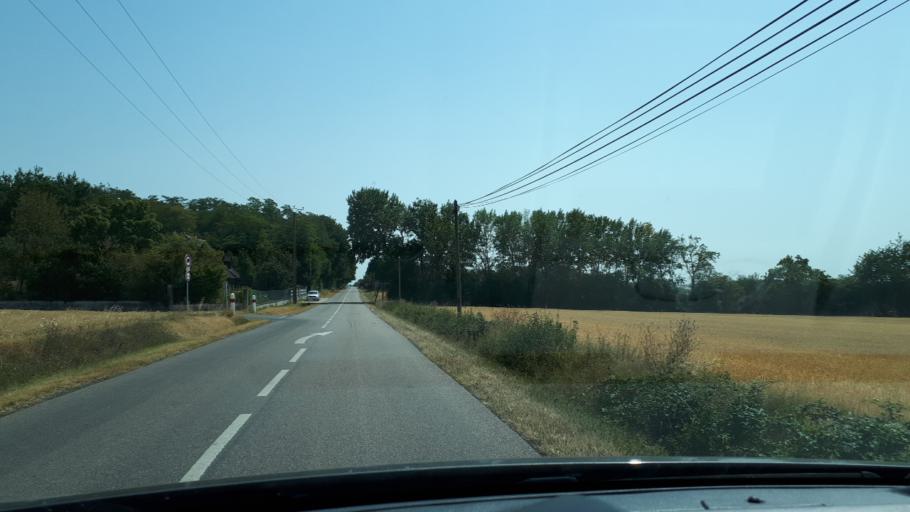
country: FR
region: Centre
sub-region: Departement du Loir-et-Cher
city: Saint-Ouen
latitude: 47.8228
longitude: 1.0676
